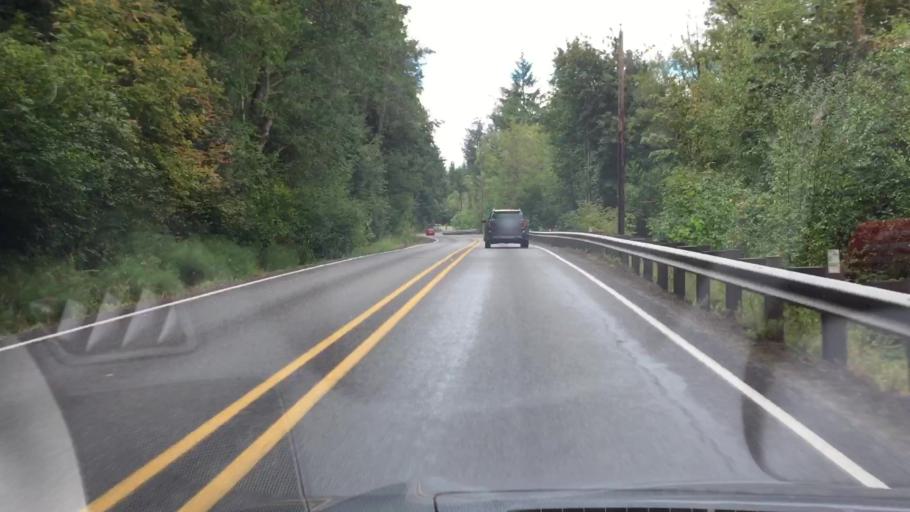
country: US
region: Washington
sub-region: Pierce County
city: Eatonville
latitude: 46.8561
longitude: -122.2592
